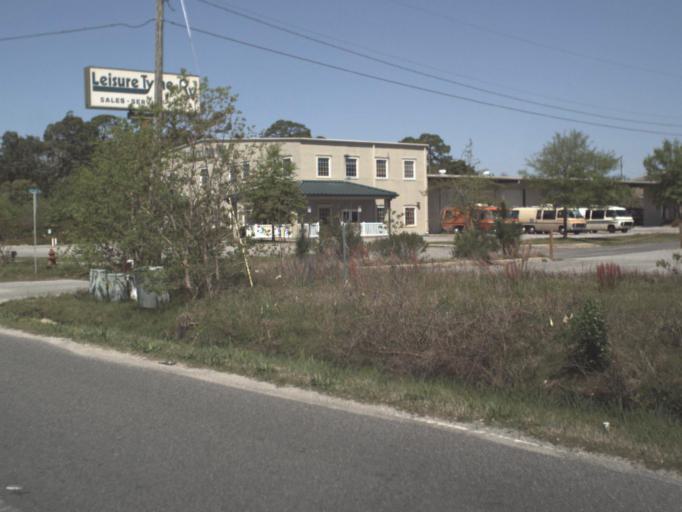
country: US
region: Florida
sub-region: Okaloosa County
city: Mary Esther
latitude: 30.4118
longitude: -86.7207
